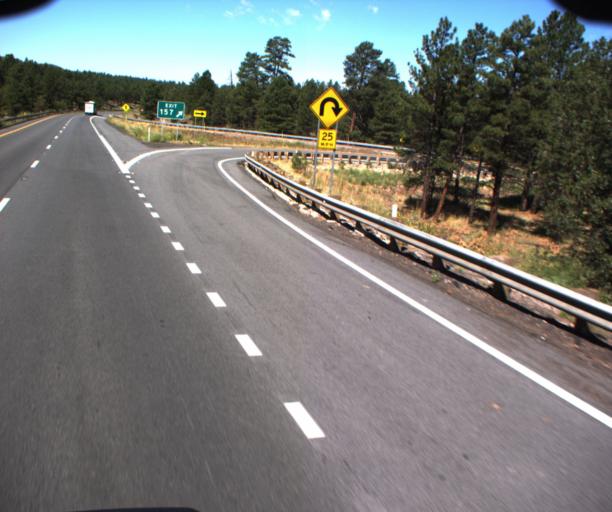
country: US
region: Arizona
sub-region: Coconino County
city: Williams
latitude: 35.2209
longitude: -112.2767
